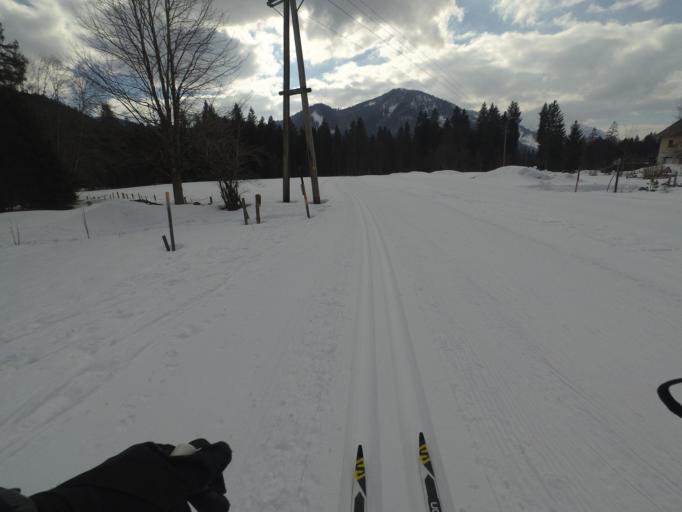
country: AT
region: Salzburg
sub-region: Politischer Bezirk Salzburg-Umgebung
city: Fuschl am See
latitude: 47.7717
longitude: 13.2917
